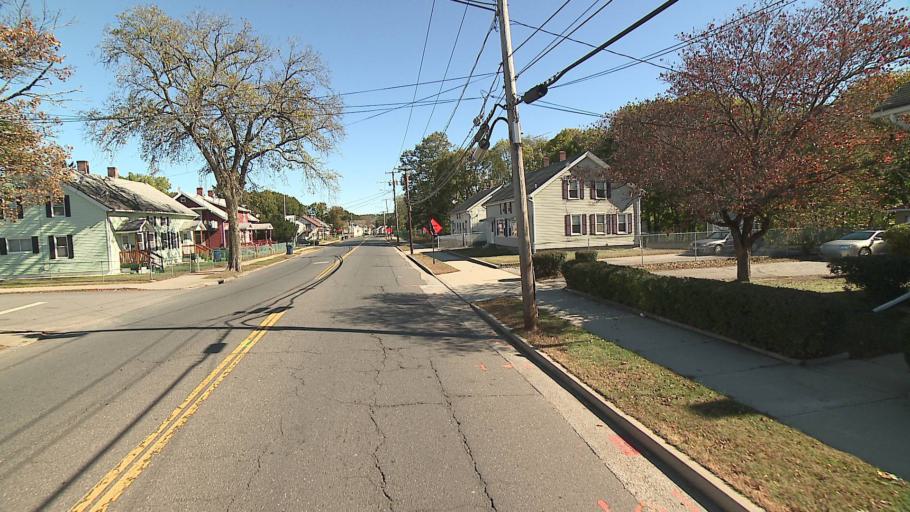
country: US
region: Connecticut
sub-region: Windham County
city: Willimantic
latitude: 41.7127
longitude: -72.2024
